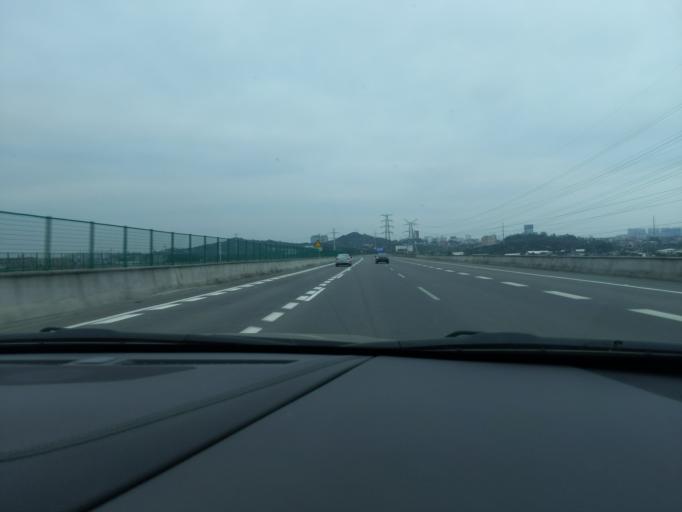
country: CN
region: Fujian
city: Shishi
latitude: 24.7497
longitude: 118.5821
